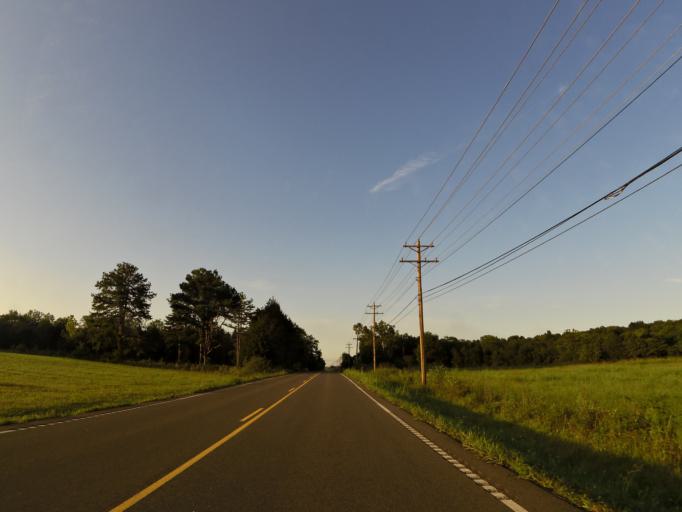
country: US
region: Tennessee
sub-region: Rhea County
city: Spring City
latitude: 35.6669
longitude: -84.6762
